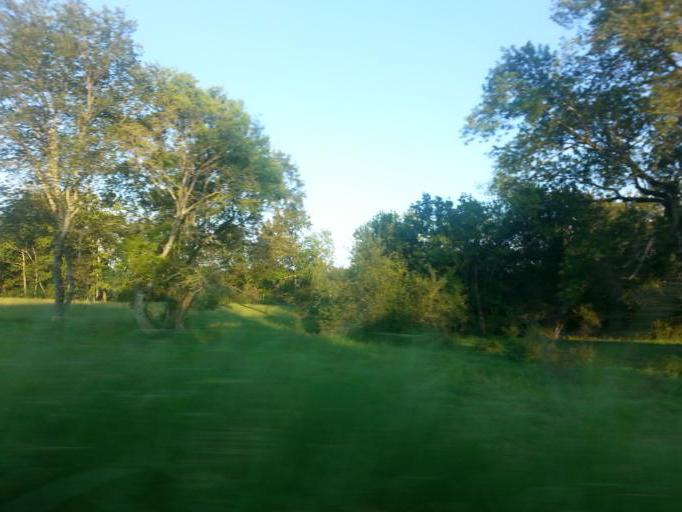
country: US
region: Tennessee
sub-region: Rhea County
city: Spring City
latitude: 35.6647
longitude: -84.6774
